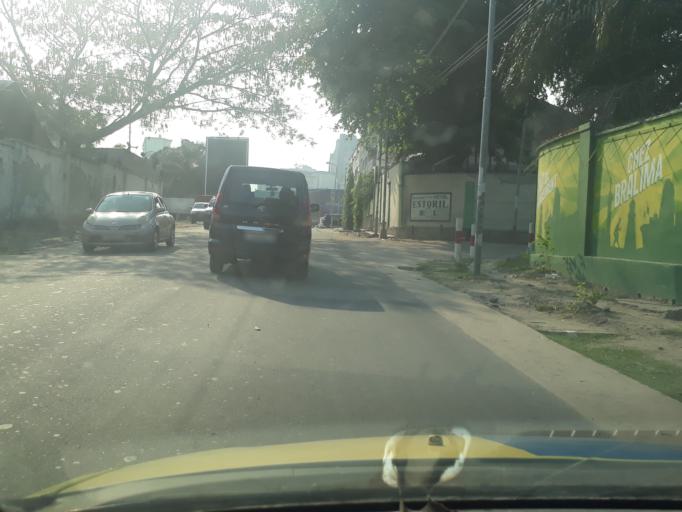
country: CD
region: Kinshasa
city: Kinshasa
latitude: -4.3047
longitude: 15.3198
